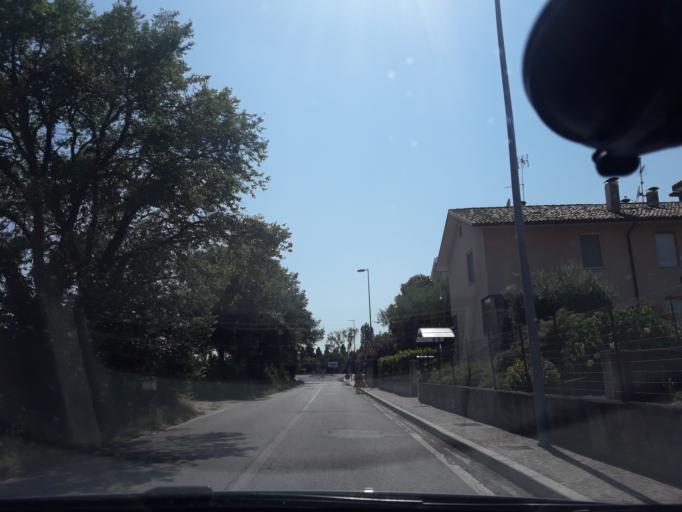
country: IT
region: Friuli Venezia Giulia
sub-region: Provincia di Udine
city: Tavagnacco
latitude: 46.1082
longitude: 13.2306
